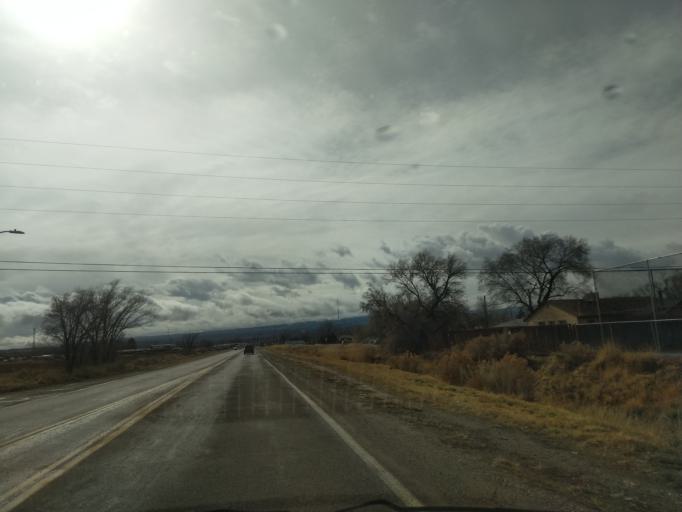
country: US
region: Colorado
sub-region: Mesa County
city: Grand Junction
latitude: 39.0741
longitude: -108.5337
